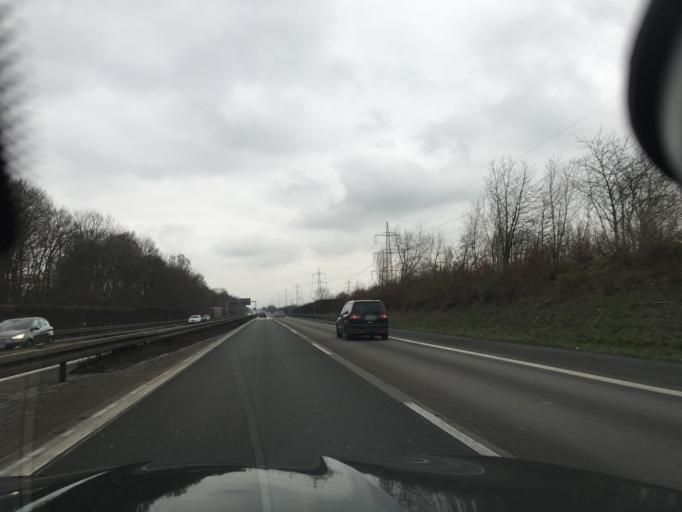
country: DE
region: North Rhine-Westphalia
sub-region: Regierungsbezirk Koln
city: Eil
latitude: 50.8786
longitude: 7.0946
